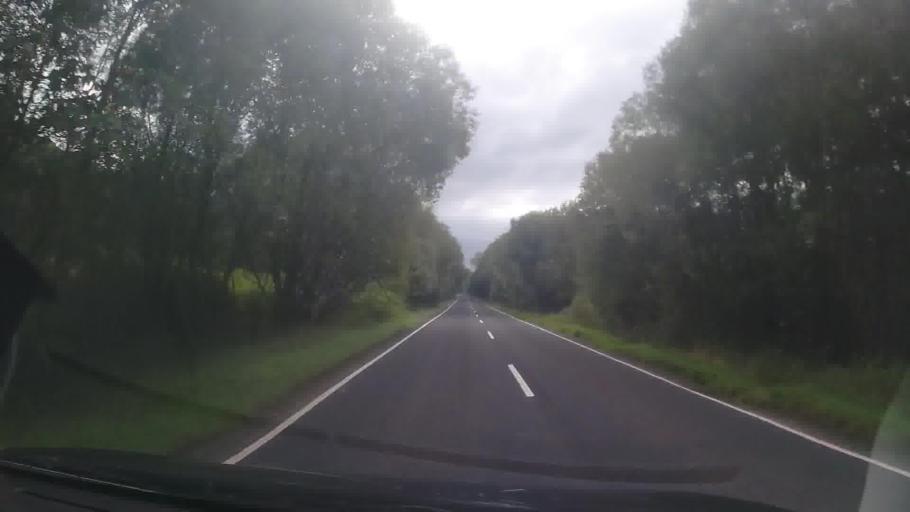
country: GB
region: Scotland
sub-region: Argyll and Bute
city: Garelochhead
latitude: 56.2435
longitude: -4.9489
